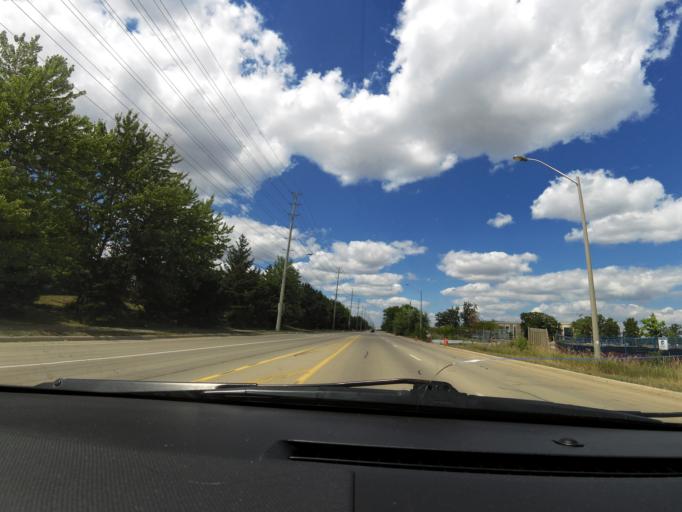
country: CA
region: Ontario
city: Oakville
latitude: 43.3827
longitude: -79.7393
